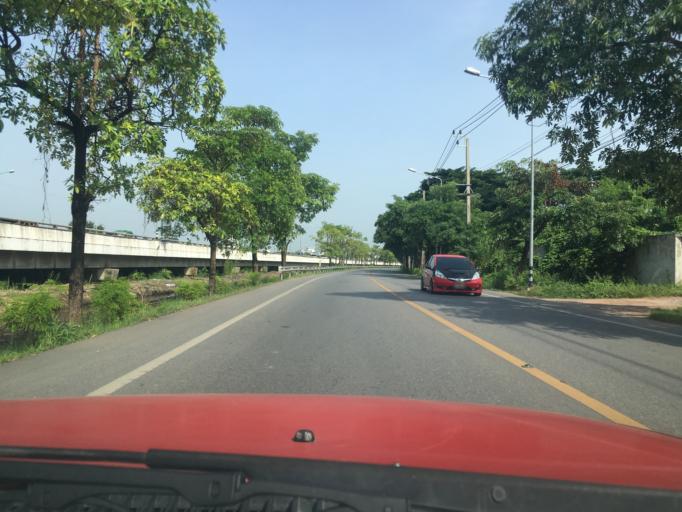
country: TH
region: Bangkok
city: Bang Khun Thian
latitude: 13.6278
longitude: 100.4227
